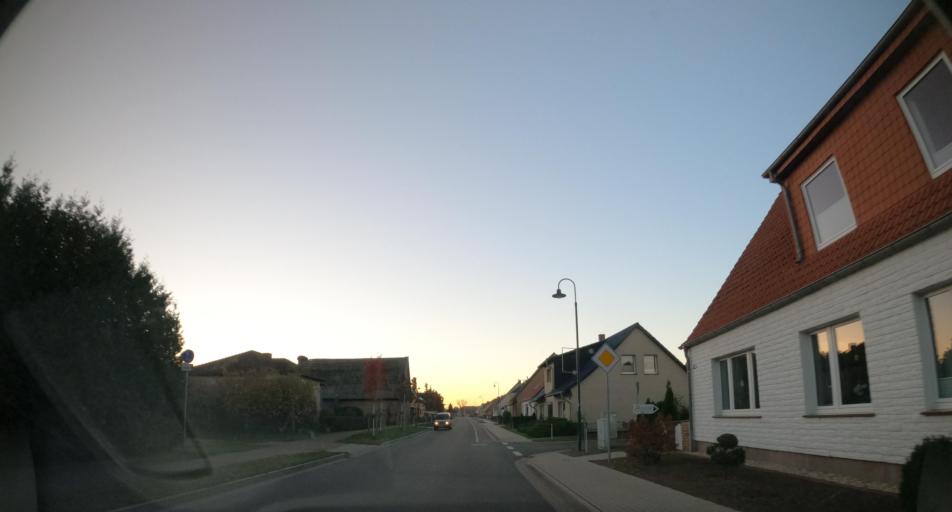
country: DE
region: Mecklenburg-Vorpommern
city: Ueckermunde
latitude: 53.7538
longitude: 14.0223
